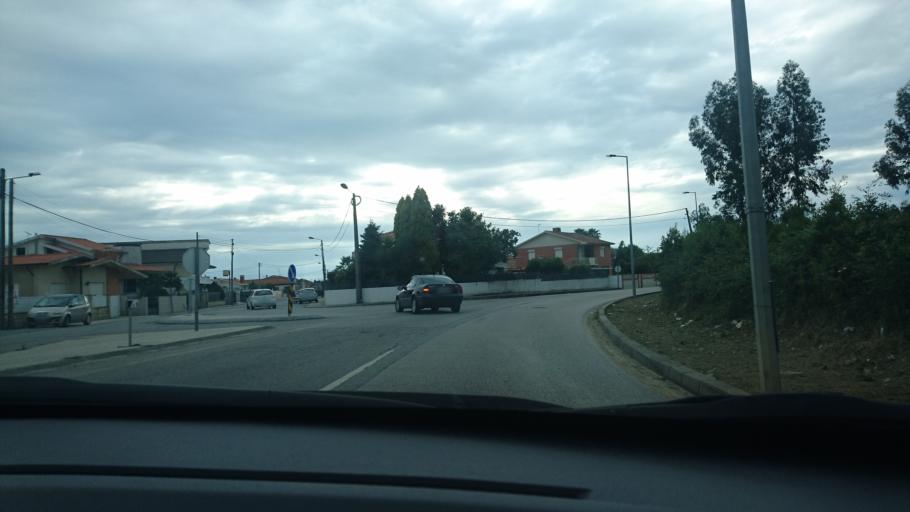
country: PT
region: Aveiro
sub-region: Santa Maria da Feira
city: Rio Meao
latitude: 40.9605
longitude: -8.5999
